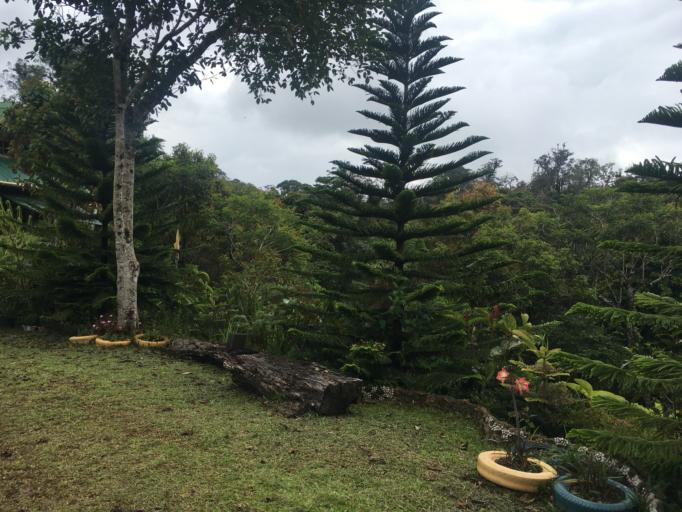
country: PH
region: Davao
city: Simod
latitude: 7.4516
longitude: 125.2552
